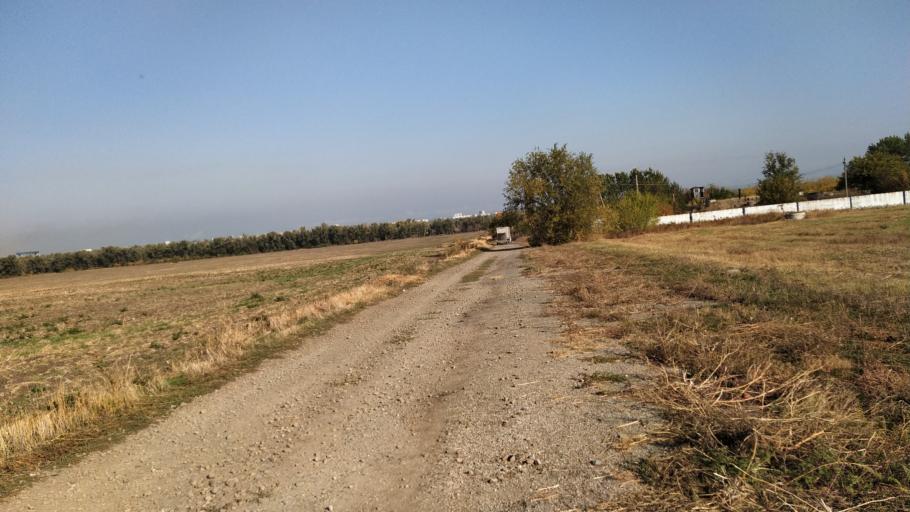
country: RU
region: Rostov
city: Bataysk
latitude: 47.0898
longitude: 39.7765
